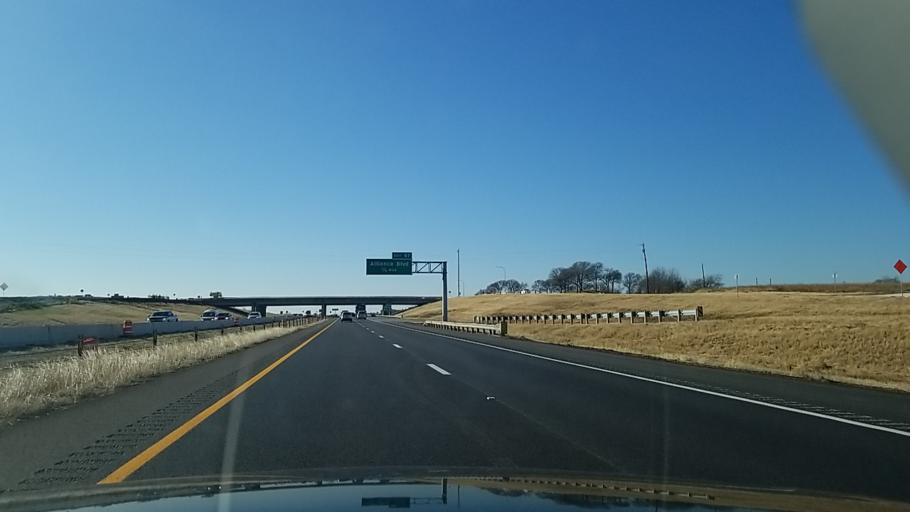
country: US
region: Texas
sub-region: Tarrant County
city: Haslet
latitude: 33.0028
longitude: -97.2915
